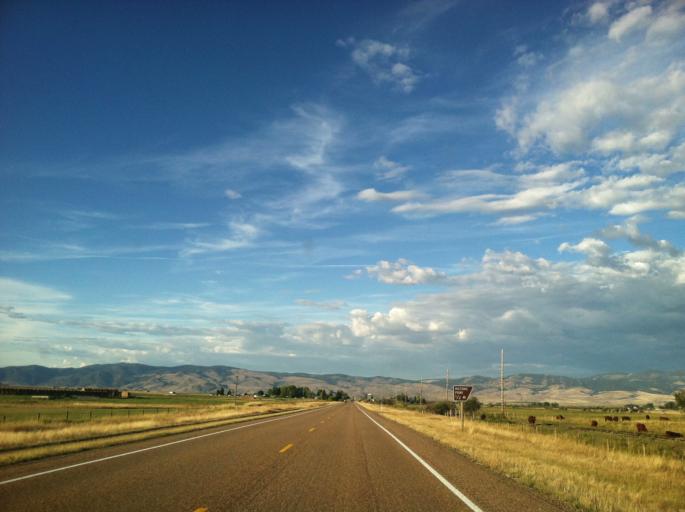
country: US
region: Montana
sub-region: Granite County
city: Philipsburg
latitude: 46.5744
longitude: -113.2040
